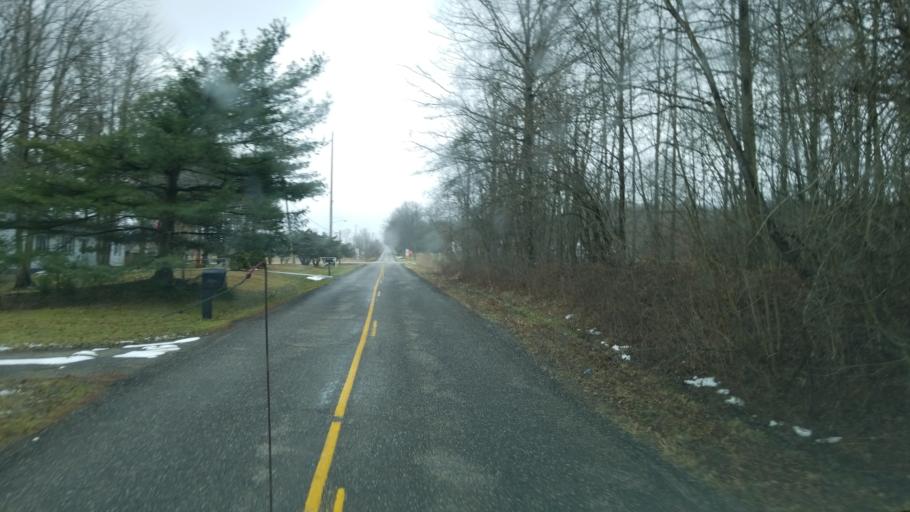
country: US
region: Ohio
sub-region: Portage County
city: Windham
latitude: 41.3098
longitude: -80.9835
